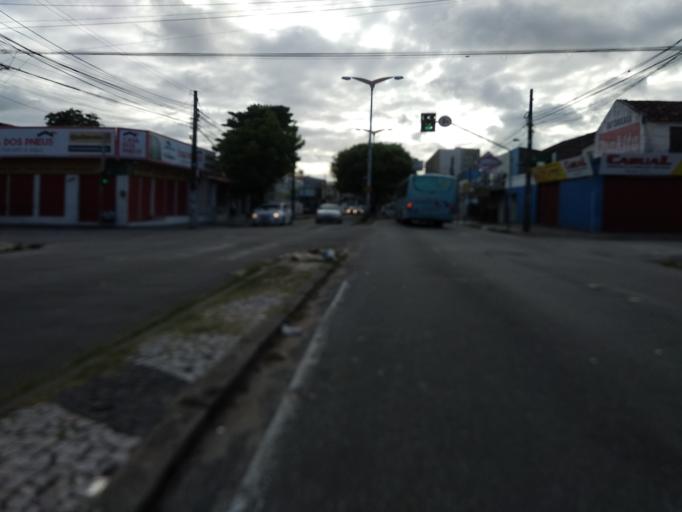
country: BR
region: Ceara
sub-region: Fortaleza
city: Fortaleza
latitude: -3.7299
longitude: -38.5361
